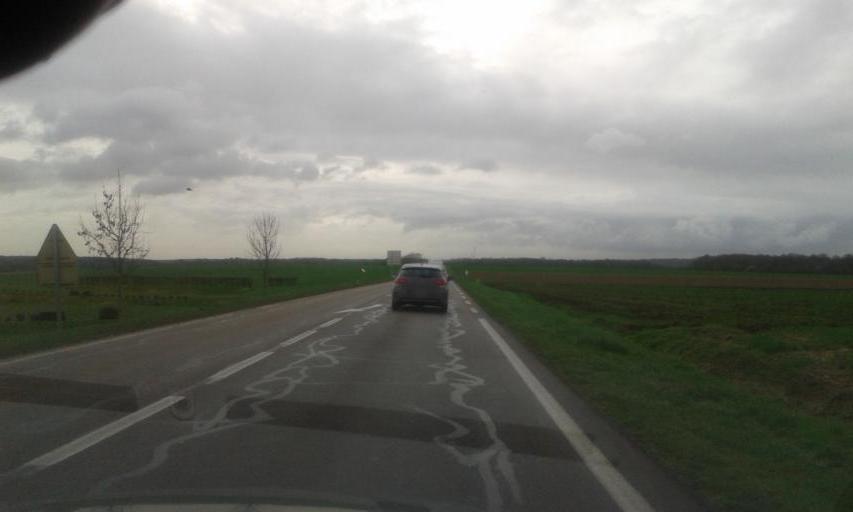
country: FR
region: Haute-Normandie
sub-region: Departement de l'Eure
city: Fleury-sur-Andelle
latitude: 49.3817
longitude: 1.3185
